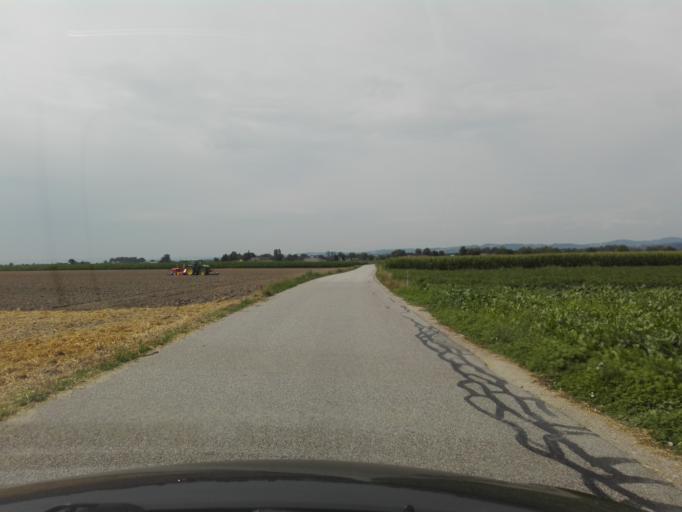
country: AT
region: Lower Austria
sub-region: Politischer Bezirk Amstetten
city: Strengberg
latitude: 48.1791
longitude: 14.7003
